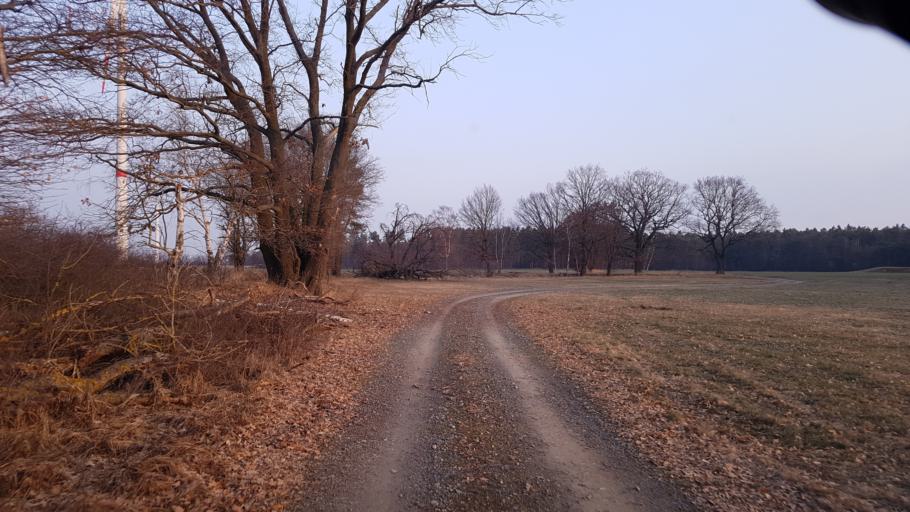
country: DE
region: Brandenburg
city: Falkenberg
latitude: 51.5734
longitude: 13.3074
